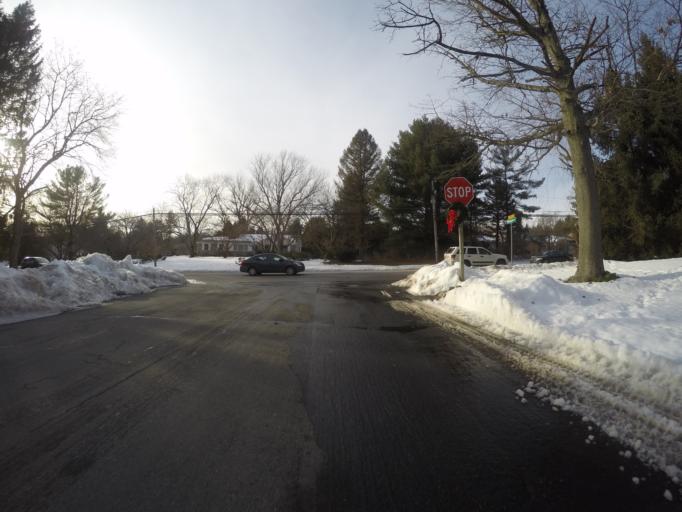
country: US
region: Maryland
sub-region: Baltimore County
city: Hampton
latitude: 39.4473
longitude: -76.5942
